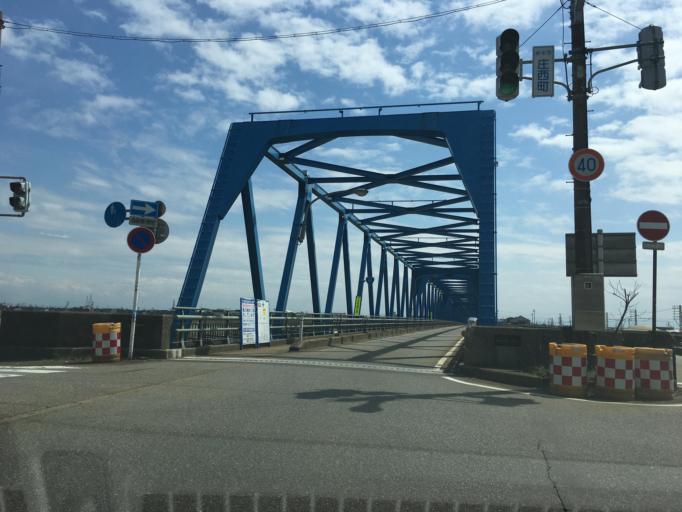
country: JP
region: Toyama
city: Nishishinminato
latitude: 36.7882
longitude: 137.0681
